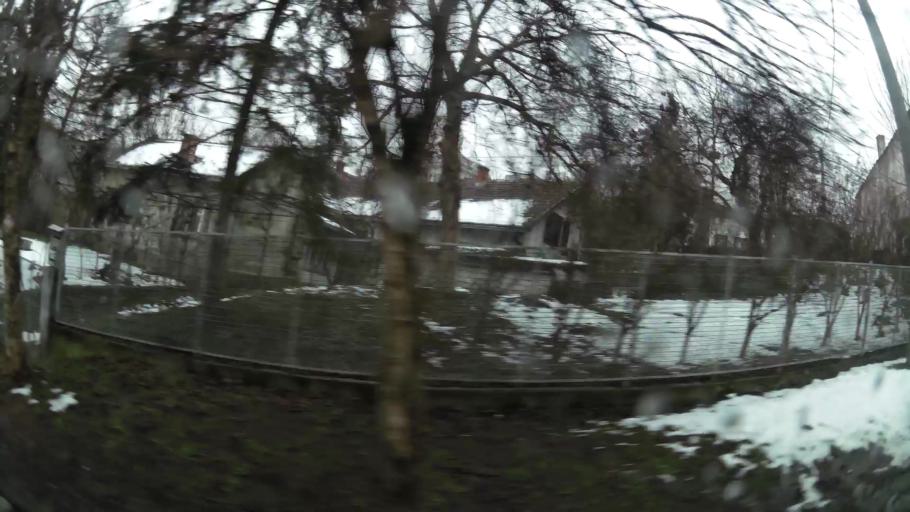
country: RS
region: Central Serbia
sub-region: Belgrade
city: Cukarica
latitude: 44.7830
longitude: 20.4138
